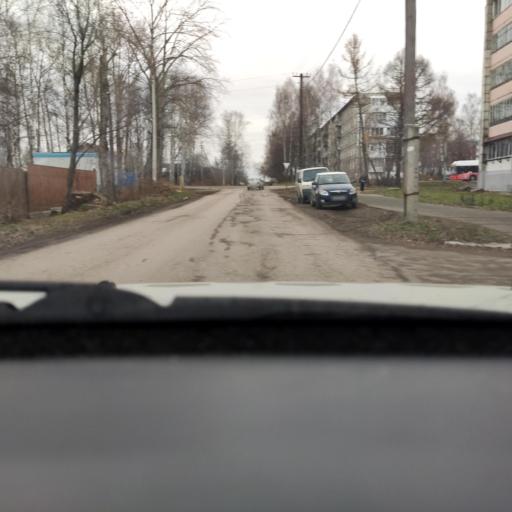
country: RU
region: Perm
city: Polazna
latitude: 58.1288
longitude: 56.3908
